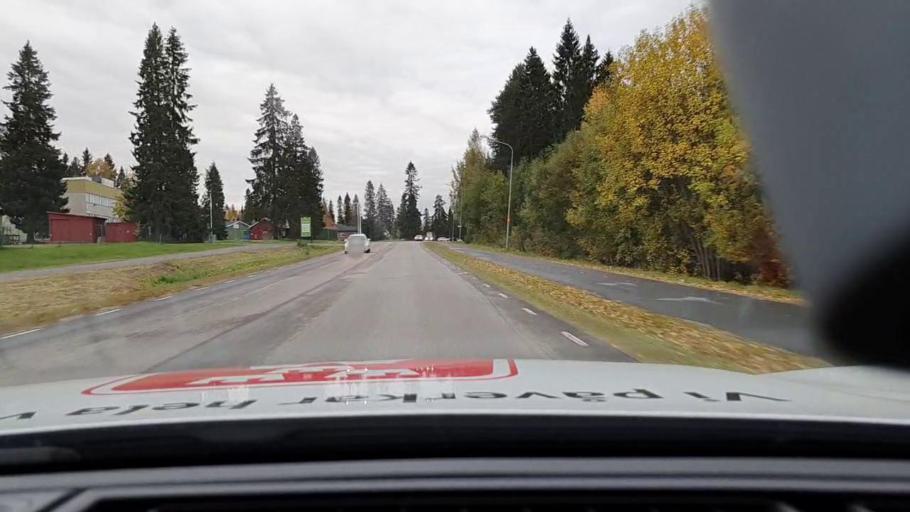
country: SE
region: Norrbotten
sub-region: Bodens Kommun
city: Boden
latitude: 65.8115
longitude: 21.6771
